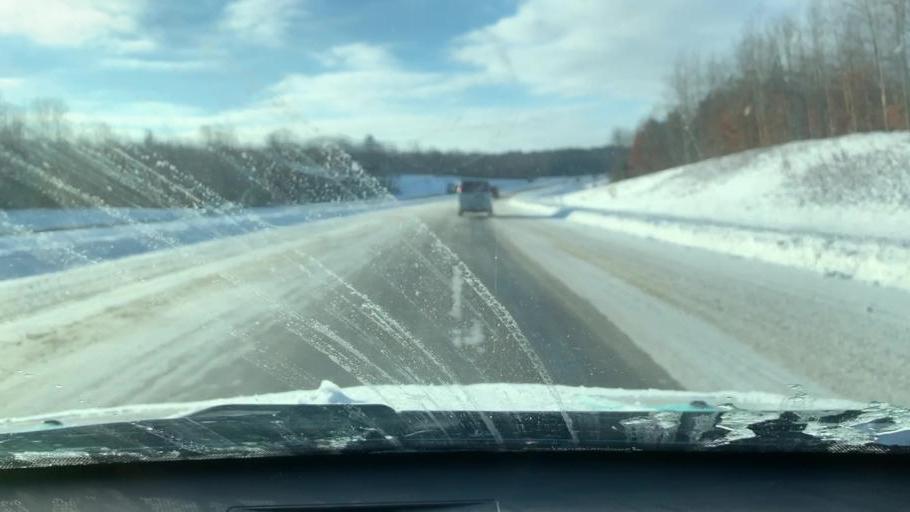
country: US
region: Michigan
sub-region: Wexford County
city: Cadillac
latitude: 44.2444
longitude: -85.3682
